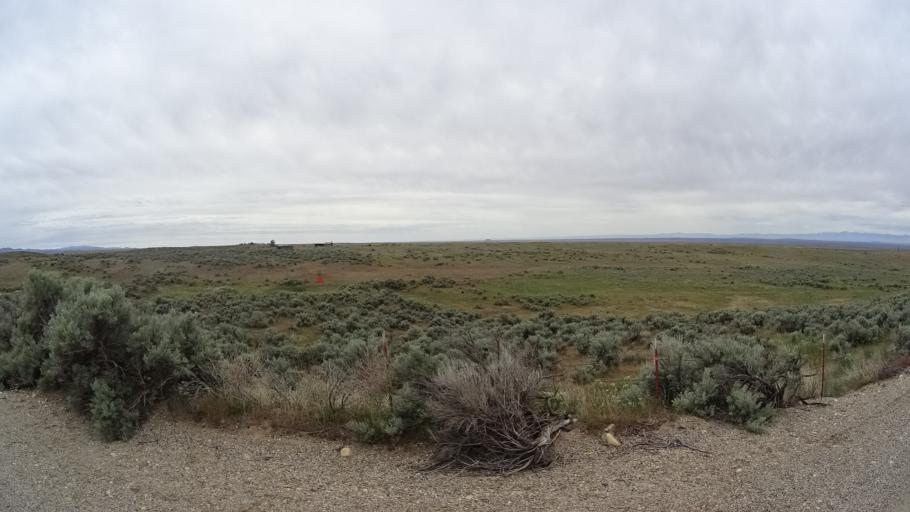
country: US
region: Idaho
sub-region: Ada County
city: Boise
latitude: 43.4782
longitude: -116.0313
